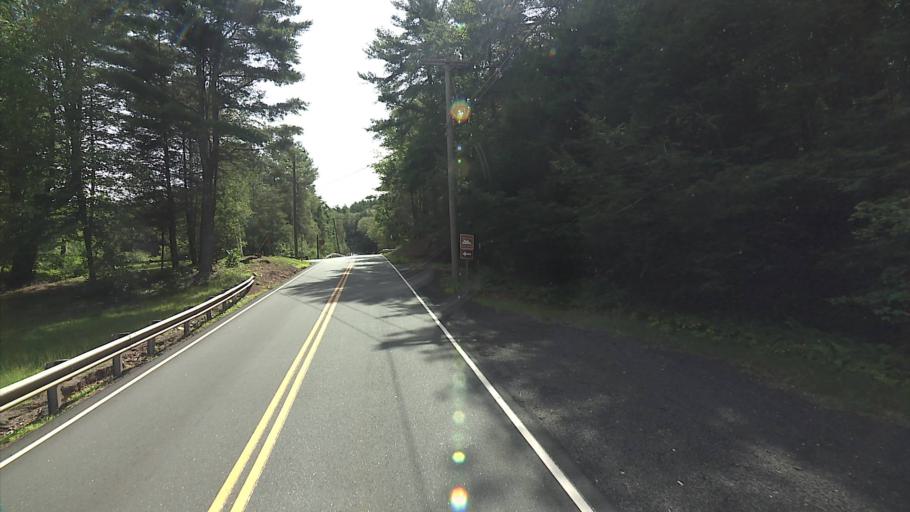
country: US
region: Massachusetts
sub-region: Hampden County
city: Holland
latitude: 41.9915
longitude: -72.1312
